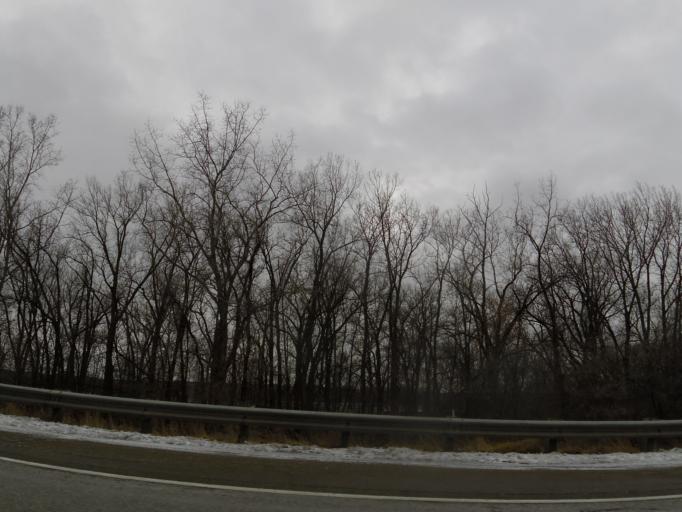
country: US
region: Minnesota
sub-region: Ramsey County
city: Maplewood
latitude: 44.9364
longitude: -93.0310
